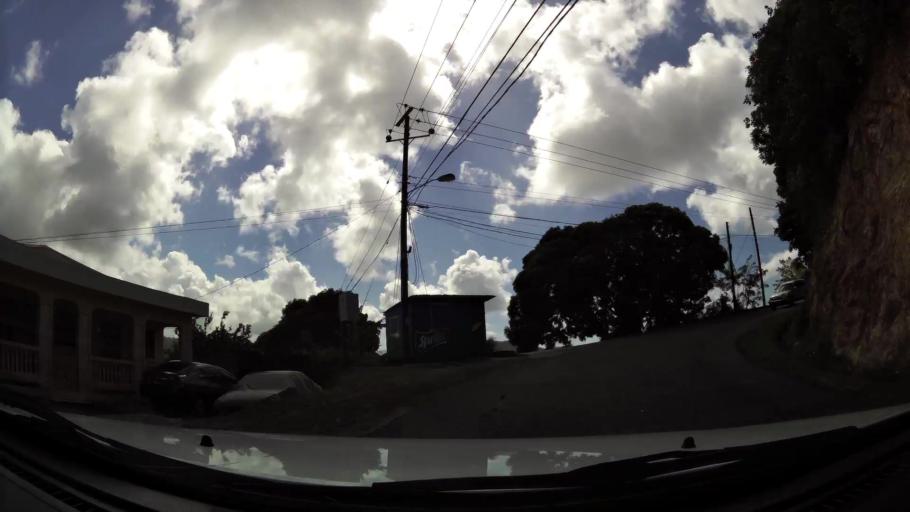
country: LC
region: Castries Quarter
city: Castries
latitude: 13.9905
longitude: -60.9969
